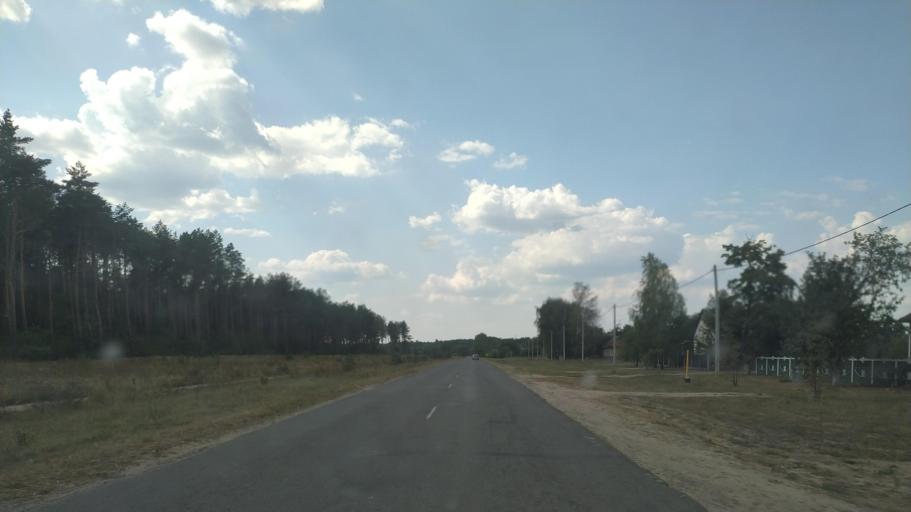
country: BY
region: Brest
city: Drahichyn
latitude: 52.1028
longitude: 25.1376
